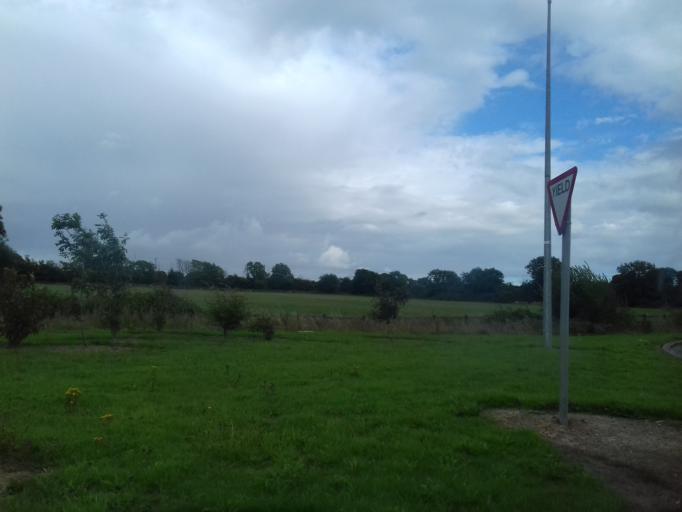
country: IE
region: Munster
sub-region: Waterford
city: Waterford
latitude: 52.2543
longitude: -7.1790
